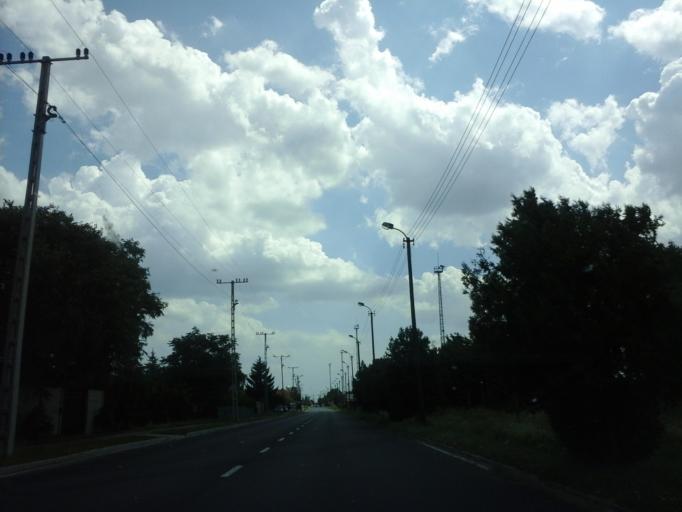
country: HU
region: Gyor-Moson-Sopron
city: Rajka
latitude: 47.9993
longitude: 17.1898
